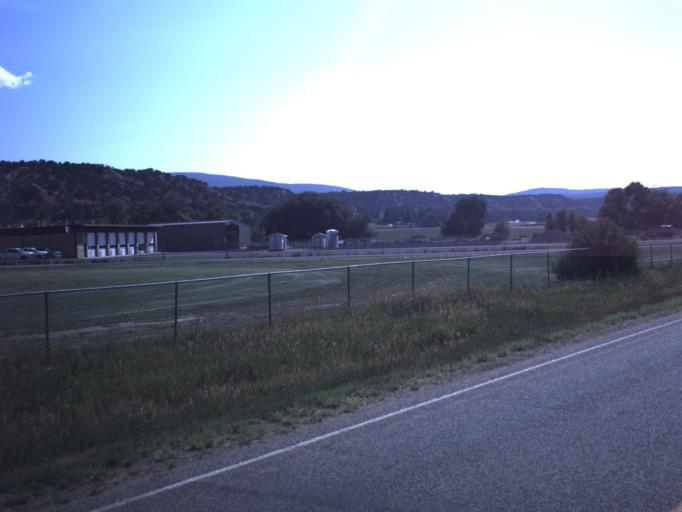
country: US
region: Utah
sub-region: Duchesne County
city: Duchesne
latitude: 40.3510
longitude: -110.7084
